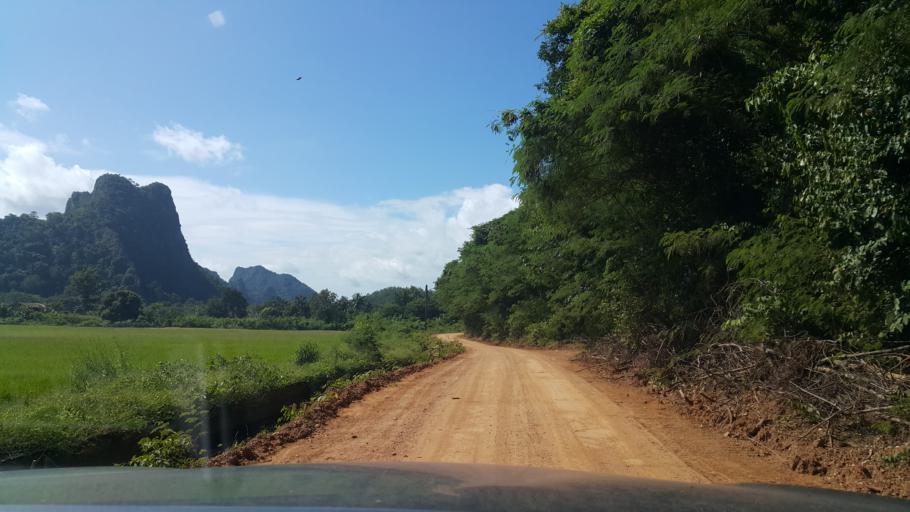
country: TH
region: Sukhothai
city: Thung Saliam
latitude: 17.3306
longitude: 99.5062
